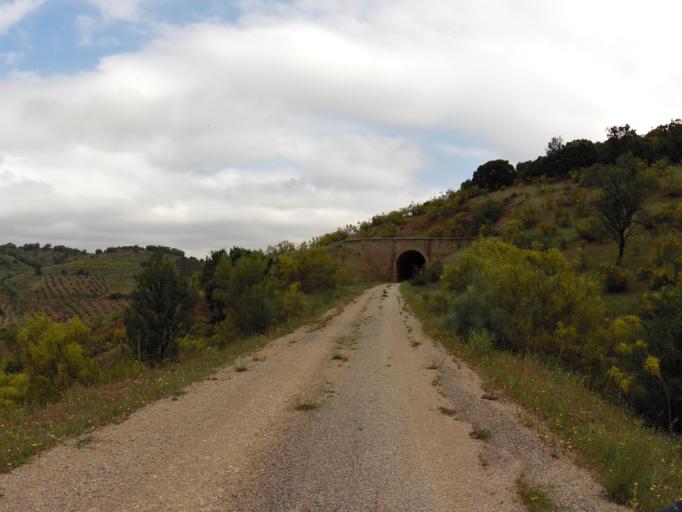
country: ES
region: Castille-La Mancha
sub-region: Provincia de Albacete
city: Alcaraz
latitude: 38.7035
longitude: -2.5017
